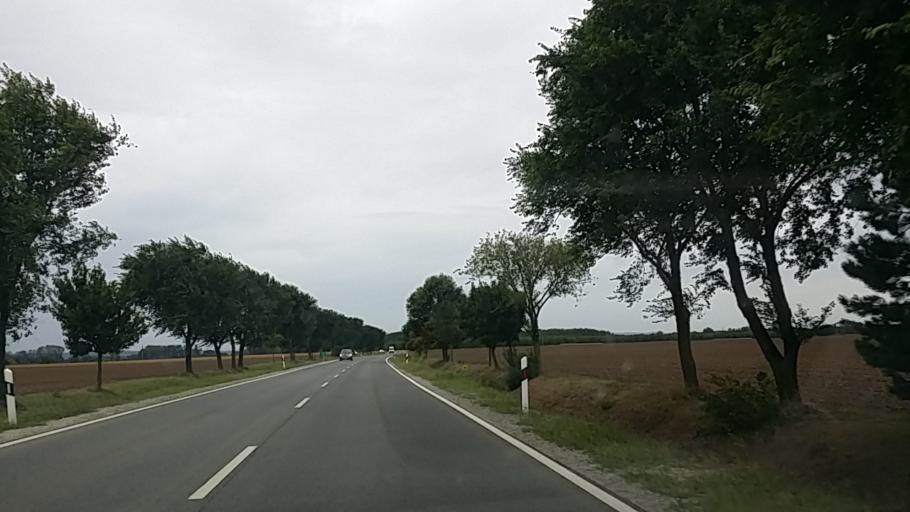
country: HU
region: Gyor-Moson-Sopron
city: Fertod
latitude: 47.5960
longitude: 16.7944
